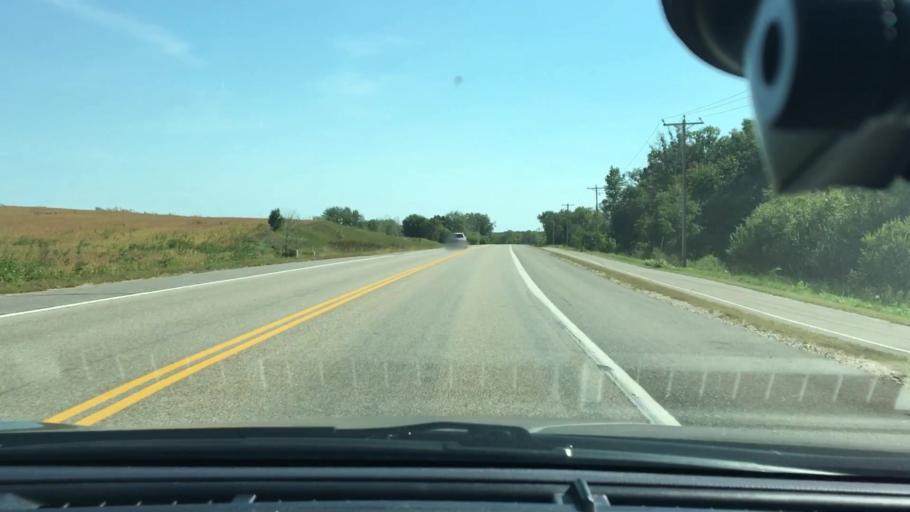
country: US
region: Minnesota
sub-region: Wright County
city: Hanover
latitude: 45.1645
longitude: -93.6750
